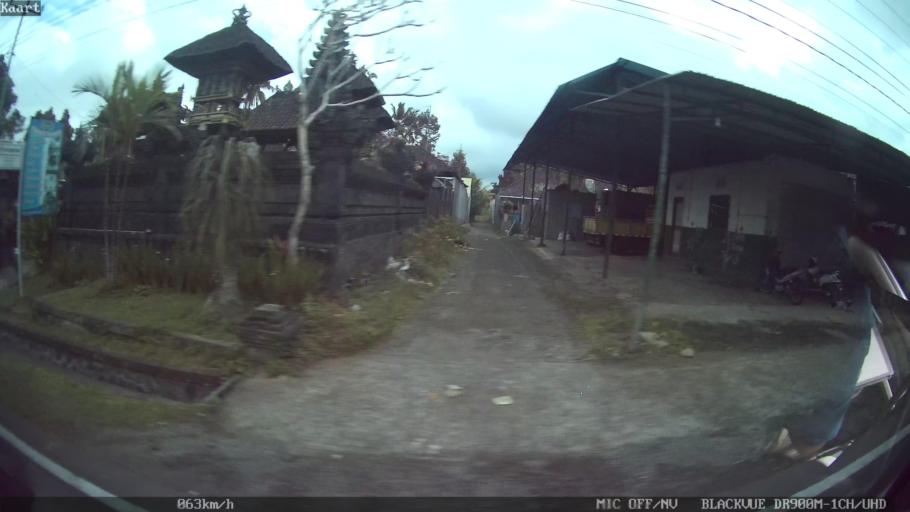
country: ID
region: Bali
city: Banjar Kubu
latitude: -8.3942
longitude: 115.4199
